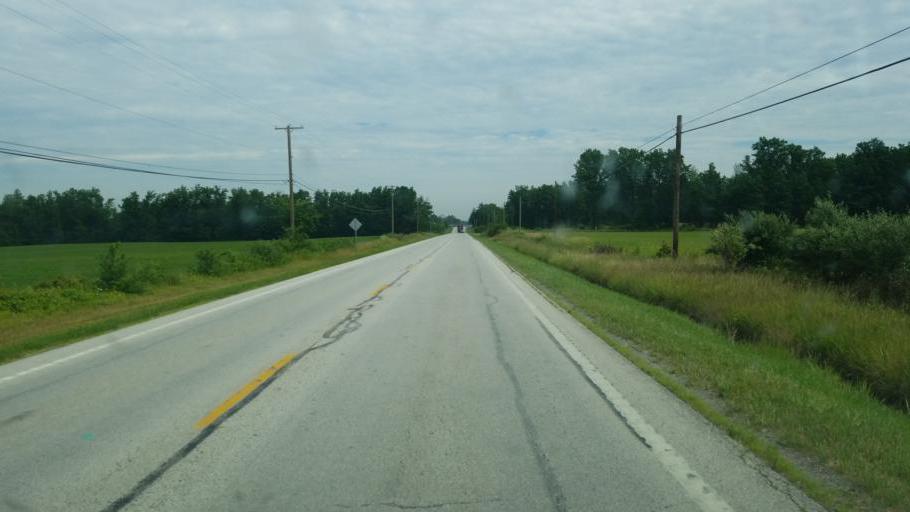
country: US
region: Ohio
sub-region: Lorain County
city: Eaton Estates
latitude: 41.3070
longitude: -82.0208
